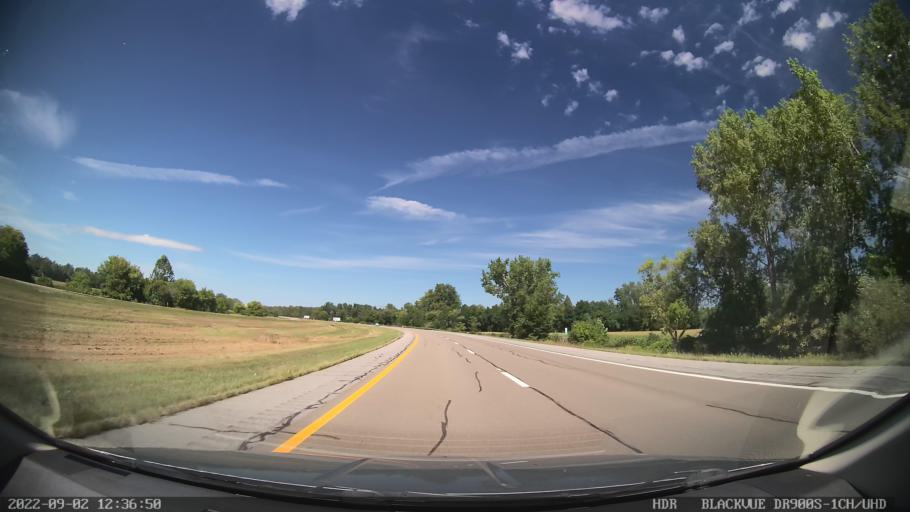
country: US
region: New York
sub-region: Livingston County
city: Mount Morris
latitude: 42.6884
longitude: -77.8006
